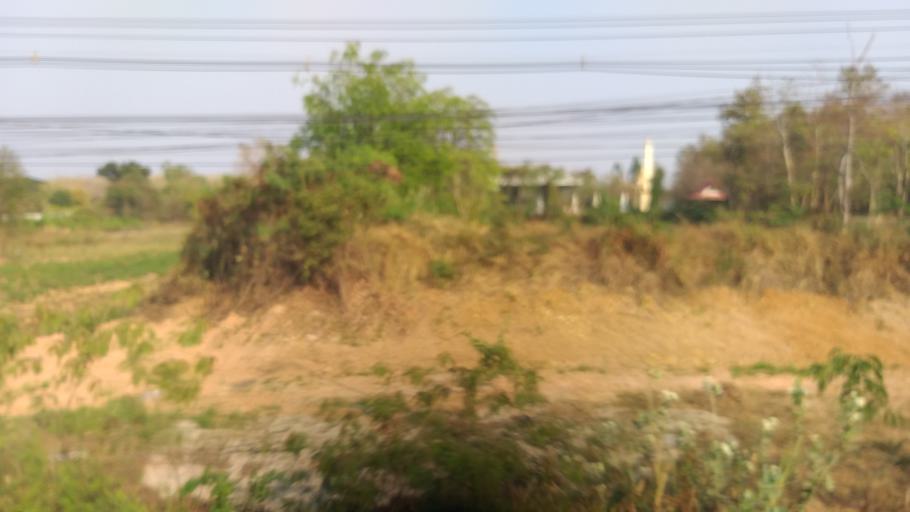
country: TH
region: Khon Kaen
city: Nam Phong
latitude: 16.7052
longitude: 102.8050
